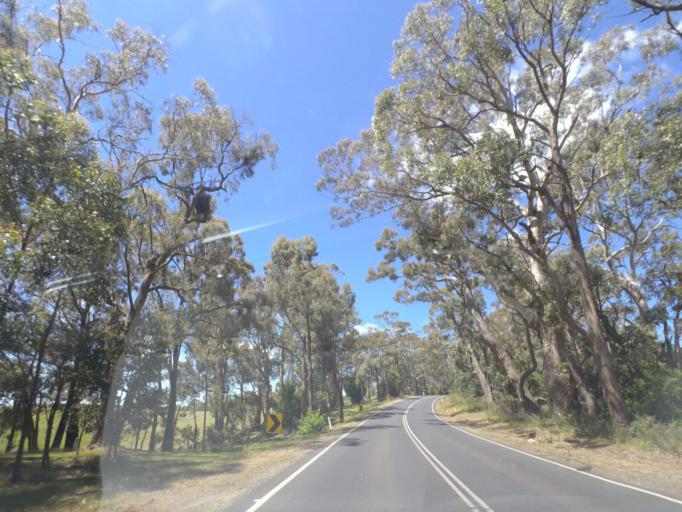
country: AU
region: Victoria
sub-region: Mount Alexander
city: Castlemaine
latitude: -37.2895
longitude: 144.2684
